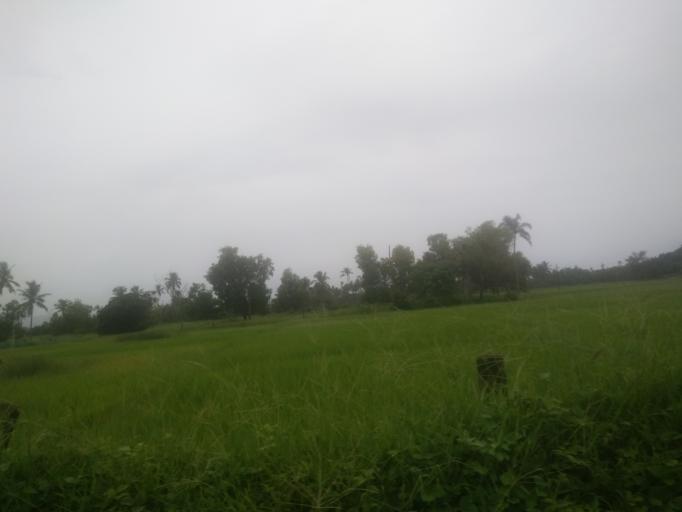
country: IN
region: Goa
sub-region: South Goa
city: Varca
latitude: 15.2056
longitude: 73.9423
